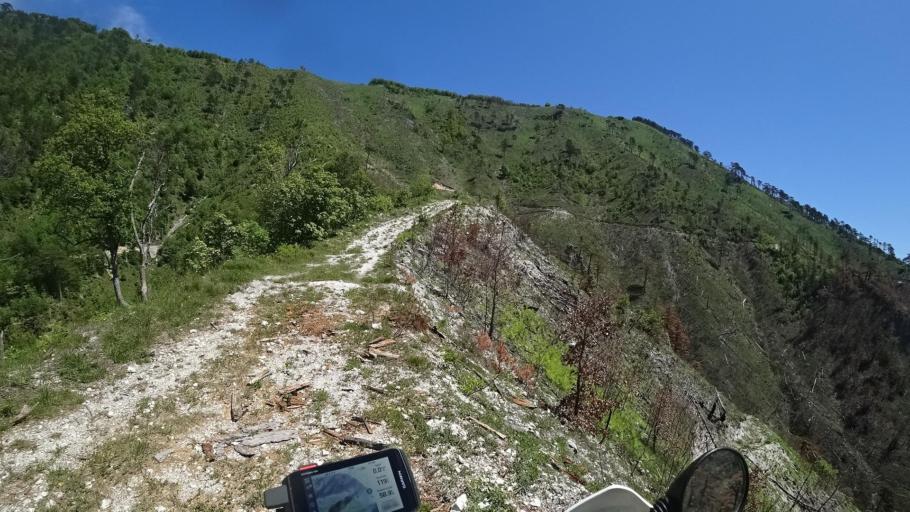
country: BA
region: Federation of Bosnia and Herzegovina
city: Polje-Bijela
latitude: 43.6233
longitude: 18.0394
